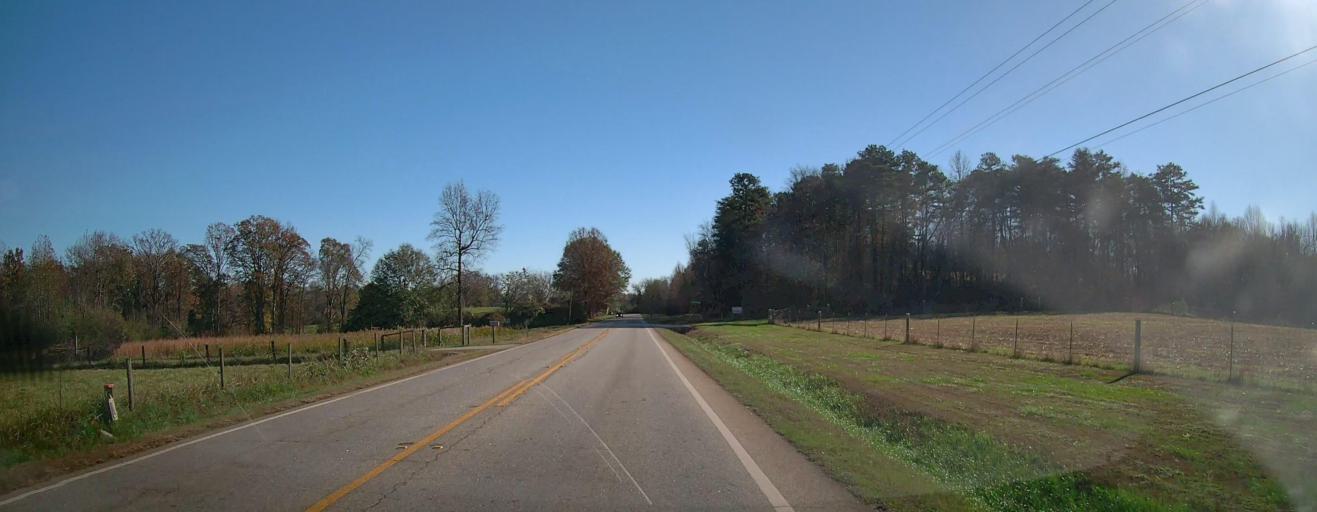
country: US
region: Georgia
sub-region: Hall County
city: Lula
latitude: 34.4634
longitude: -83.7347
